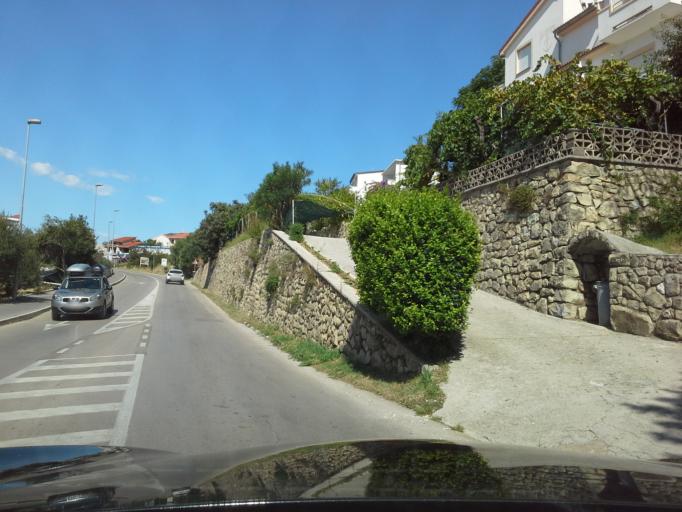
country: HR
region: Primorsko-Goranska
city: Banjol
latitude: 44.7596
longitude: 14.7685
